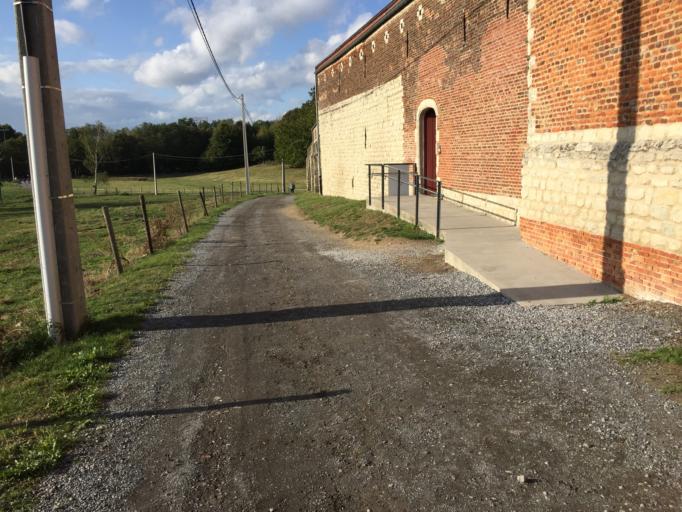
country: BE
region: Wallonia
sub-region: Province du Brabant Wallon
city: Braine-l'Alleud
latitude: 50.6704
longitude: 4.3947
